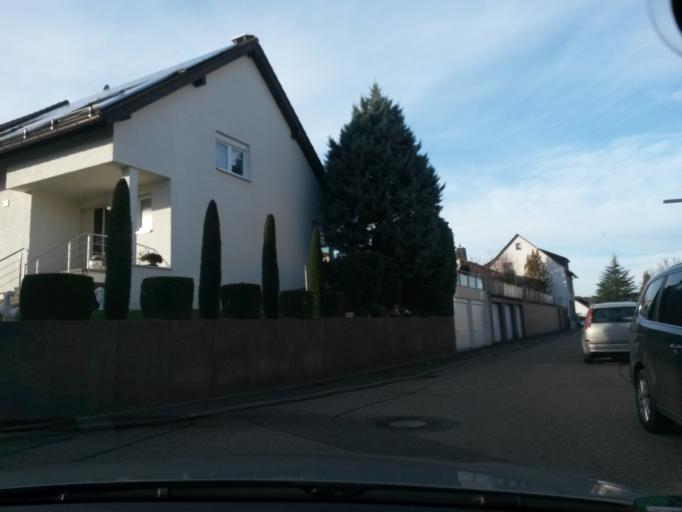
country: DE
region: Baden-Wuerttemberg
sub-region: Karlsruhe Region
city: Neuenburg
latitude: 48.8993
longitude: 8.5759
